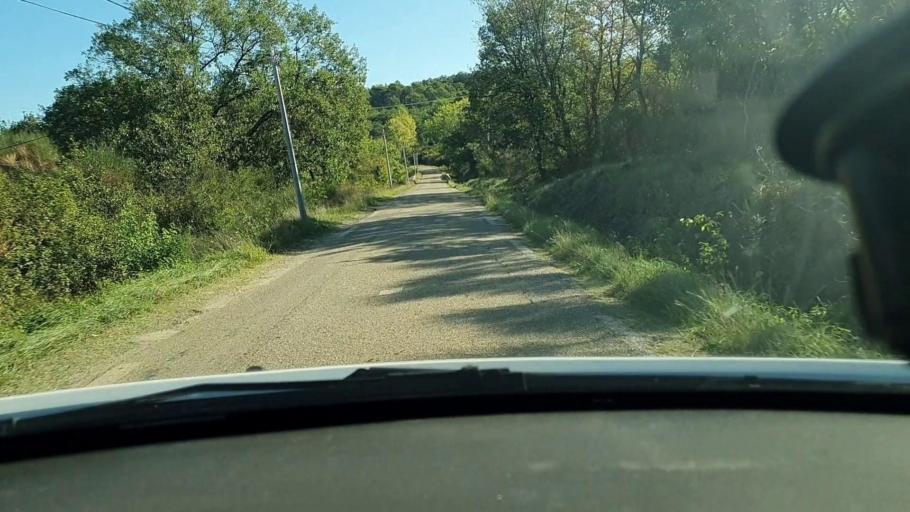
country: FR
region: Languedoc-Roussillon
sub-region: Departement du Gard
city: Saint-Julien-de-Peyrolas
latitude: 44.2546
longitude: 4.5189
